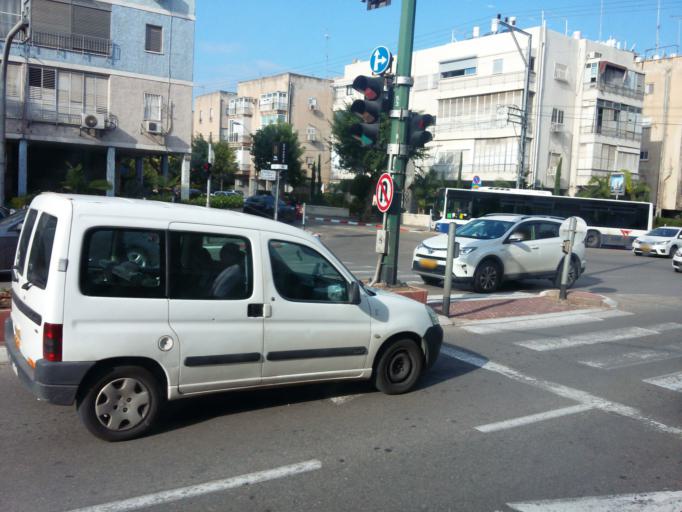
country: IL
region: Tel Aviv
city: Tel Aviv
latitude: 32.0930
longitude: 34.7947
